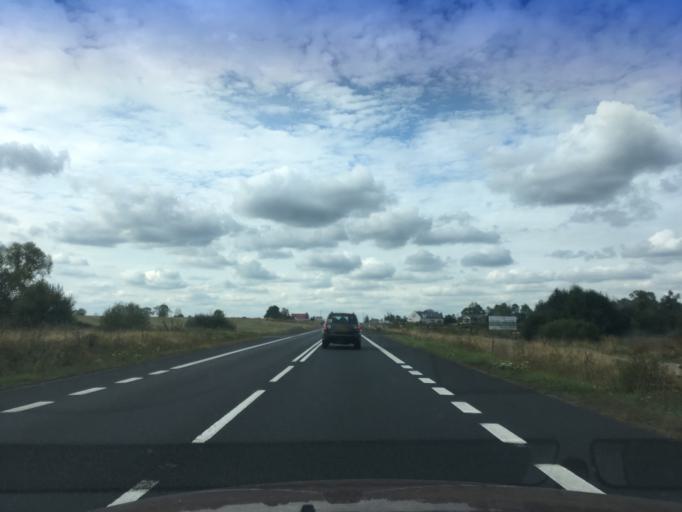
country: PL
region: Lower Silesian Voivodeship
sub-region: Powiat lwowecki
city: Gryfow Slaski
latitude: 51.0048
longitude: 15.4519
